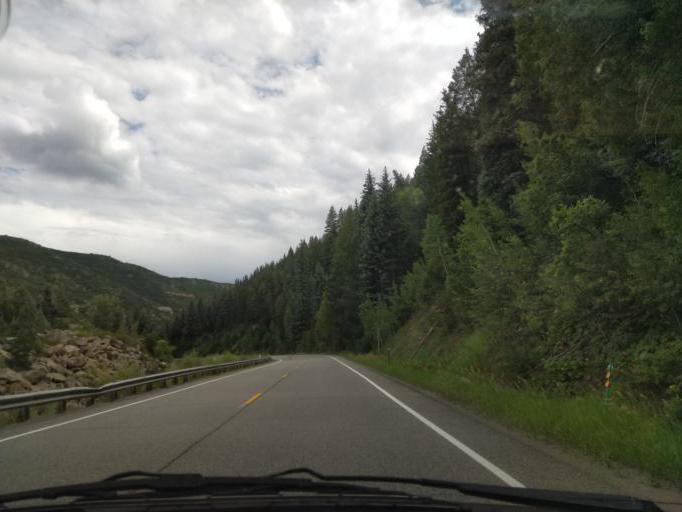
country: US
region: Colorado
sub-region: Delta County
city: Paonia
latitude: 38.9947
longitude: -107.3566
